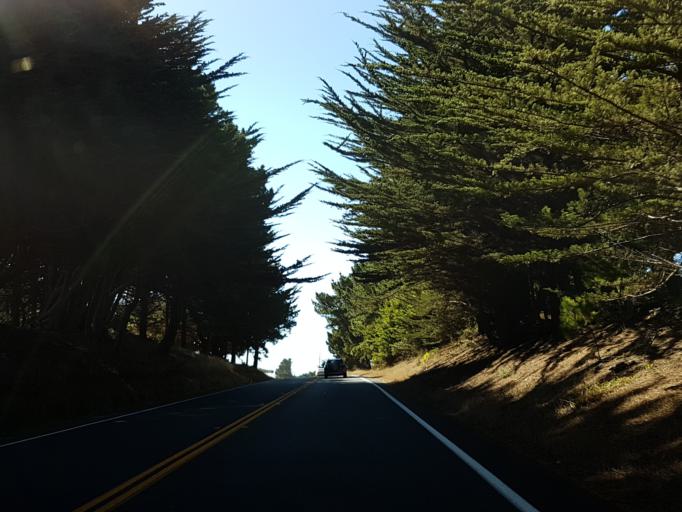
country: US
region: California
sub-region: Mendocino County
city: Boonville
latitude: 39.0302
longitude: -123.6883
